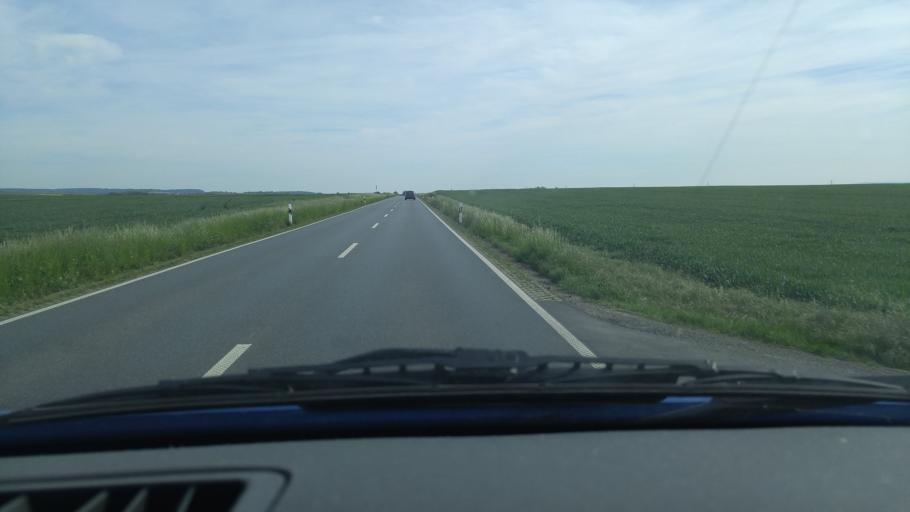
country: DE
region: Hesse
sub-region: Regierungsbezirk Darmstadt
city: Wolfersheim
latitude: 50.3657
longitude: 8.7977
